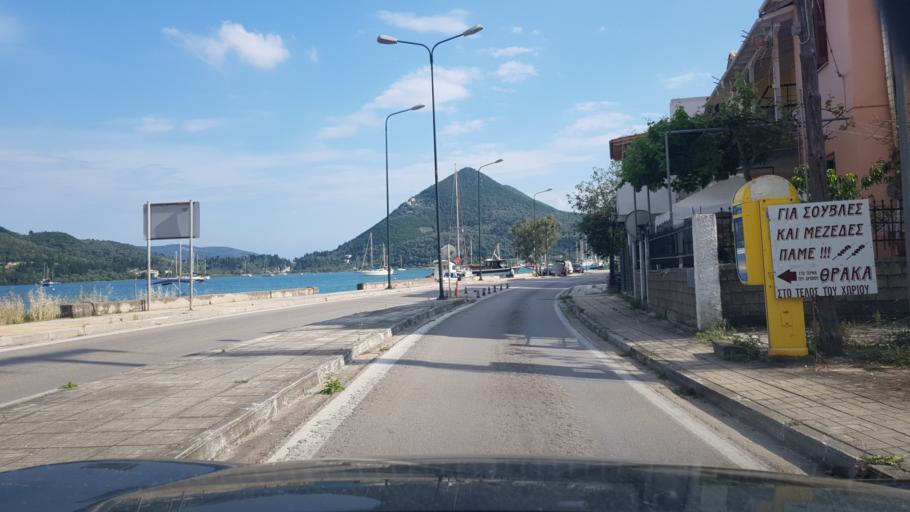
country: GR
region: Ionian Islands
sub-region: Lefkada
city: Nidri
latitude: 38.6899
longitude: 20.6986
